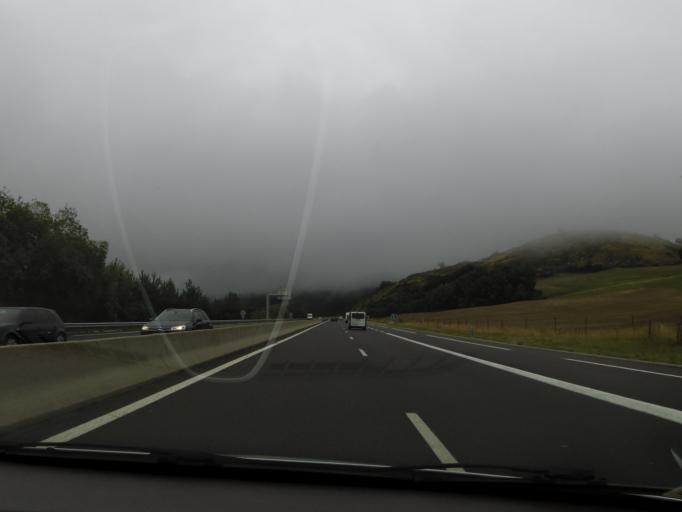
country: FR
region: Languedoc-Roussillon
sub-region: Departement de la Lozere
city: Marvejols
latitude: 44.5811
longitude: 3.2496
